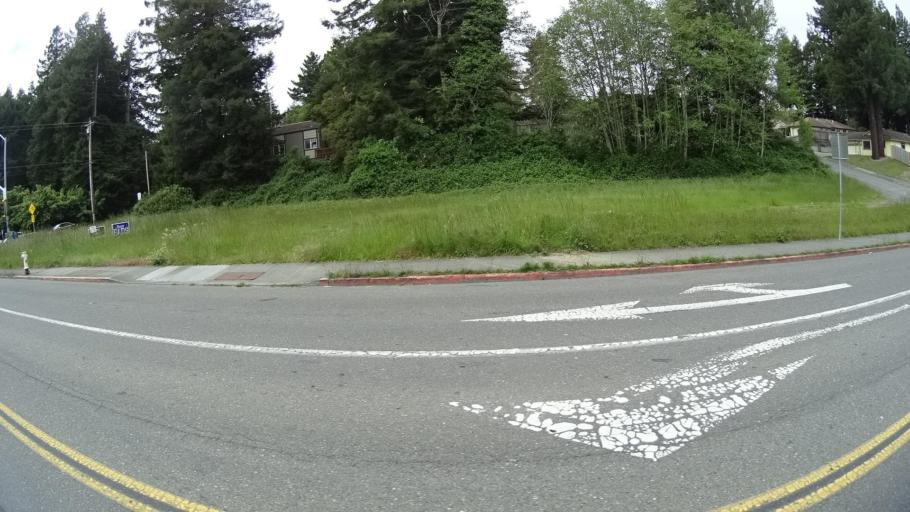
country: US
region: California
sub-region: Humboldt County
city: Cutten
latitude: 40.7808
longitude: -124.1396
